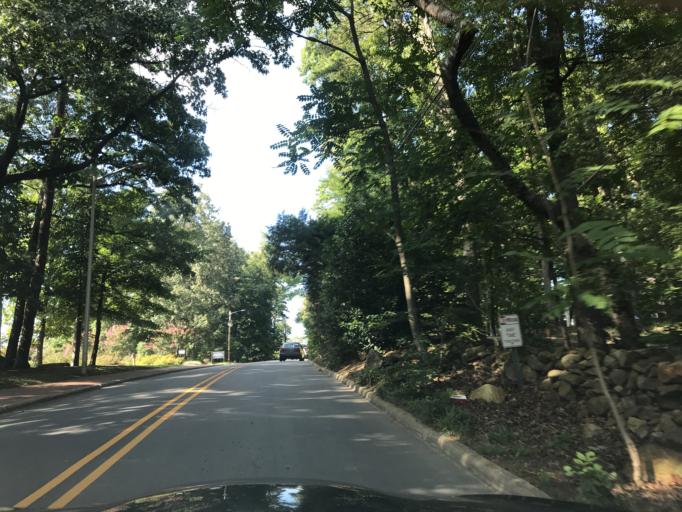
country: US
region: North Carolina
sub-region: Orange County
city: Chapel Hill
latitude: 35.9084
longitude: -79.0416
